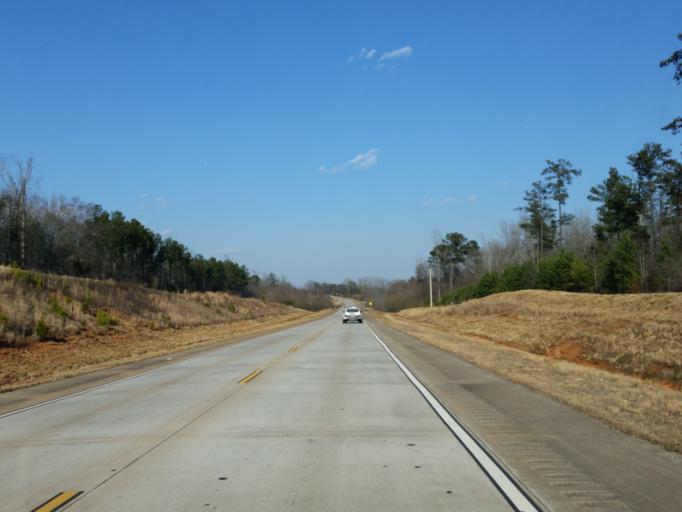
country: US
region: Georgia
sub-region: Lamar County
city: Barnesville
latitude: 33.0347
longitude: -84.1403
